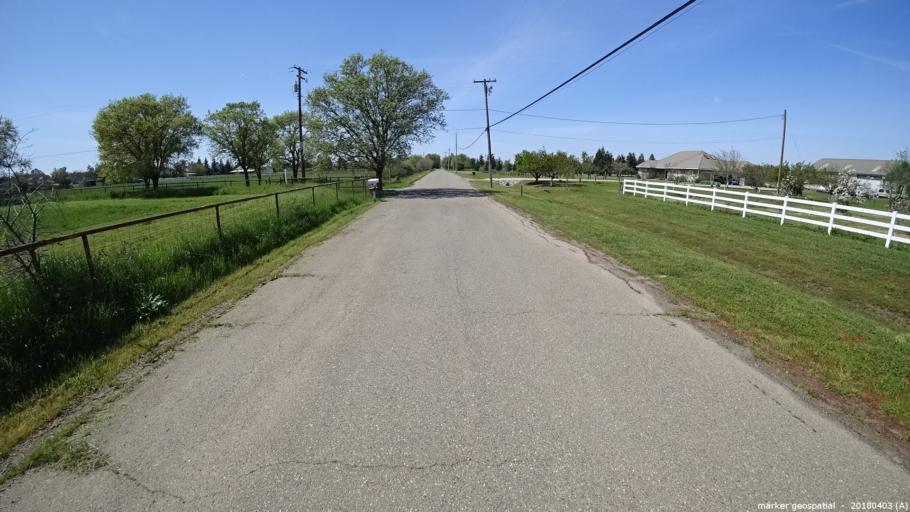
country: US
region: California
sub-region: Sacramento County
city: Wilton
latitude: 38.3943
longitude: -121.2557
